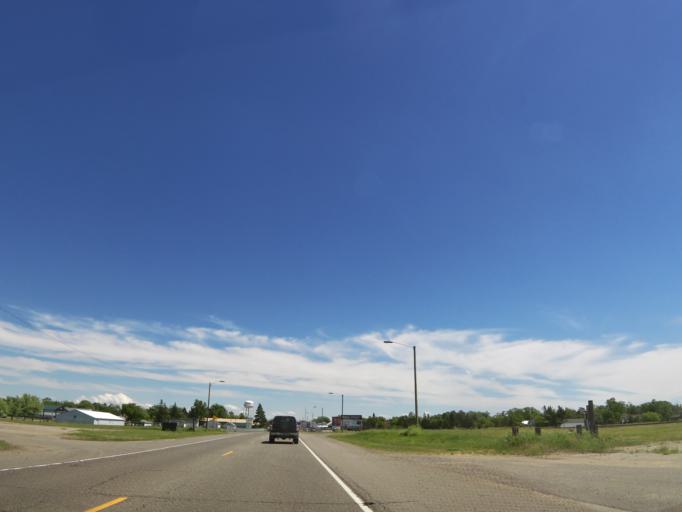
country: US
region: Minnesota
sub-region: Wadena County
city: Wadena
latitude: 46.4457
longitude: -95.1456
